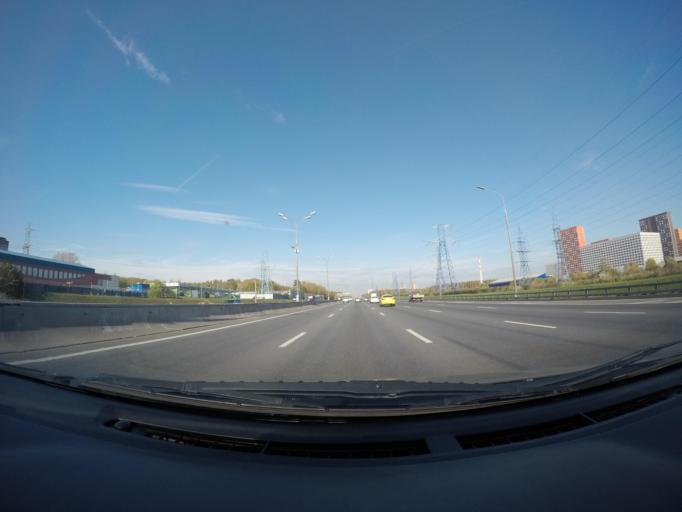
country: RU
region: Moscow
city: Ivanovskoye
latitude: 55.7814
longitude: 37.8423
